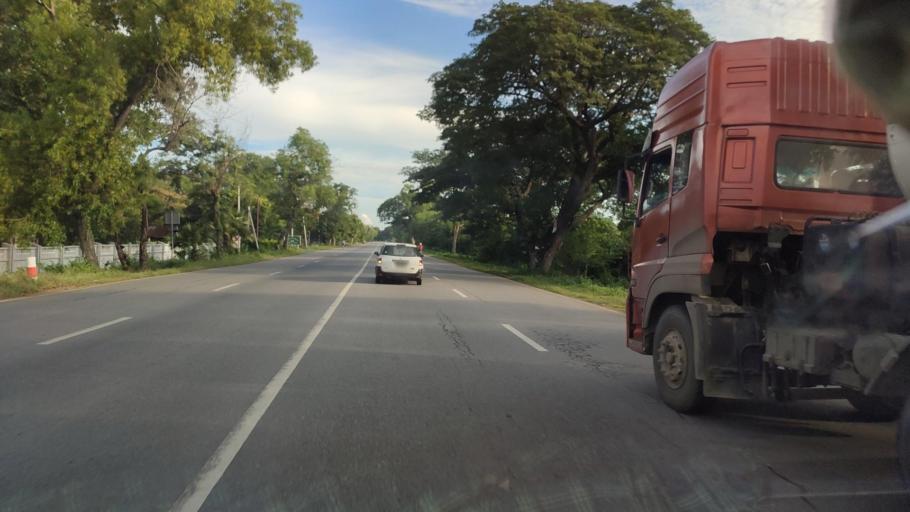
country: MM
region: Mandalay
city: Yamethin
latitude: 20.1571
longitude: 96.1913
